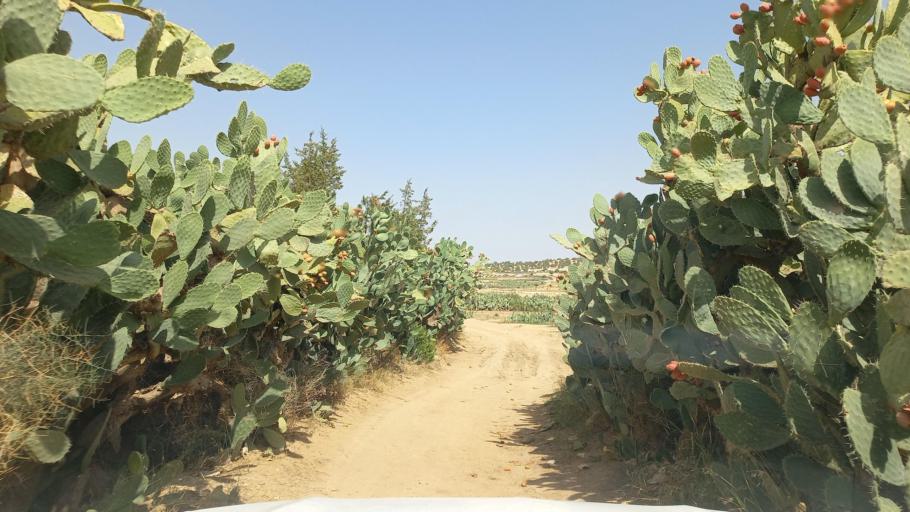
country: TN
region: Al Qasrayn
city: Sbiba
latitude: 35.3867
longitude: 8.9612
